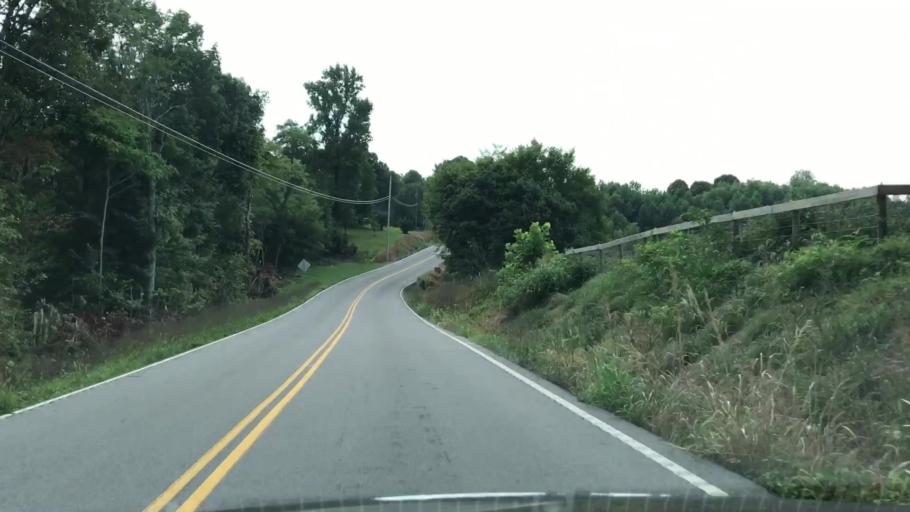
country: US
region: Tennessee
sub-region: Sumner County
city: Westmoreland
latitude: 36.5142
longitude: -86.1791
